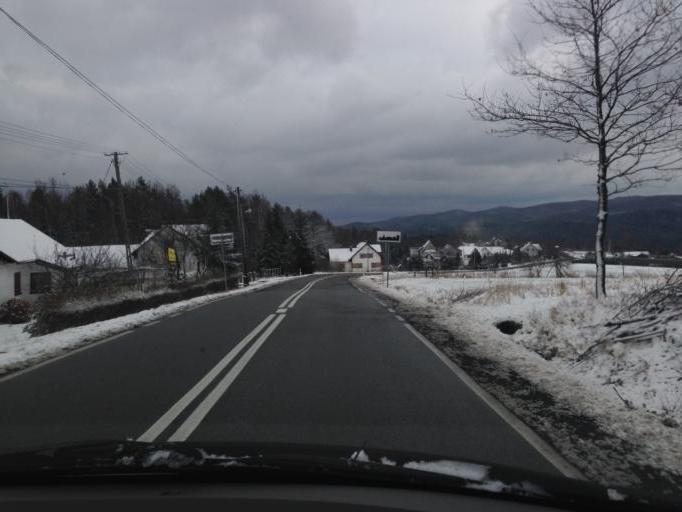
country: PL
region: Lesser Poland Voivodeship
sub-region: Powiat bochenski
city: Nowy Wisnicz
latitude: 49.8523
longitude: 20.4829
